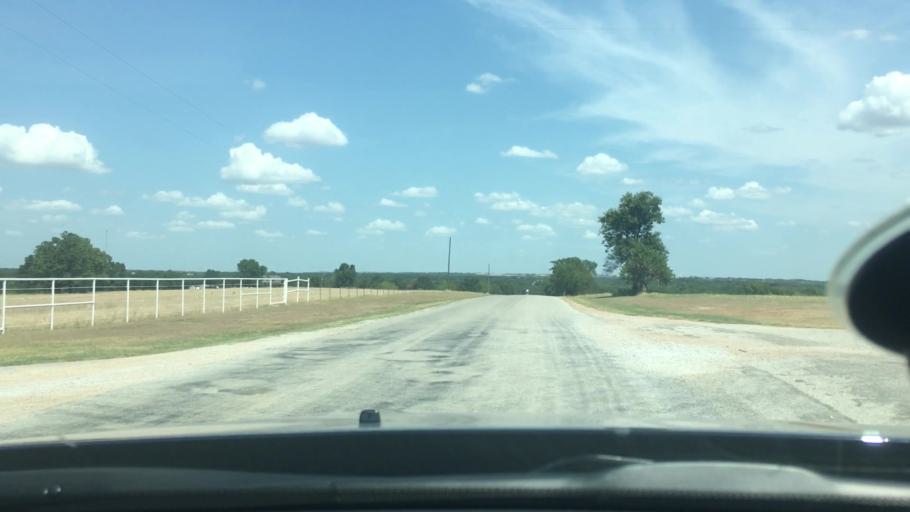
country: US
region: Oklahoma
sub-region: Love County
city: Marietta
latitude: 34.0457
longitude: -97.1957
